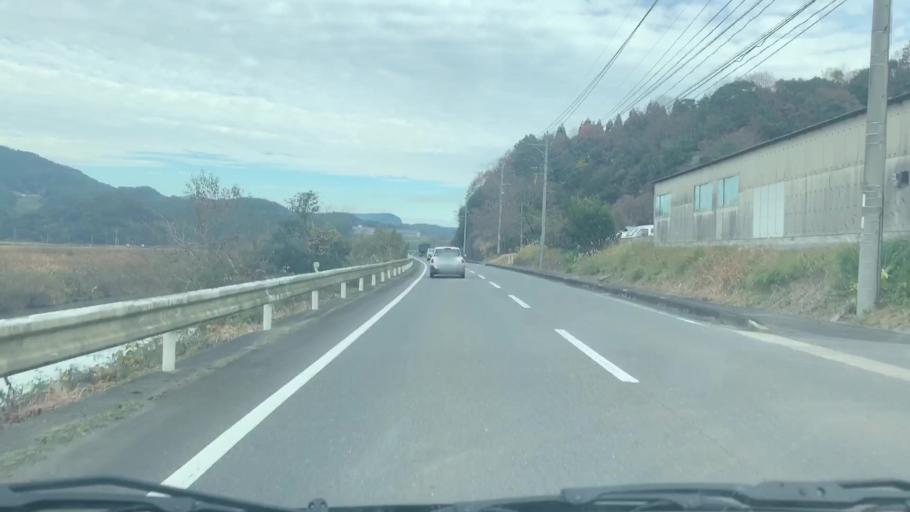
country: JP
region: Saga Prefecture
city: Imaricho-ko
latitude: 33.2747
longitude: 129.9649
